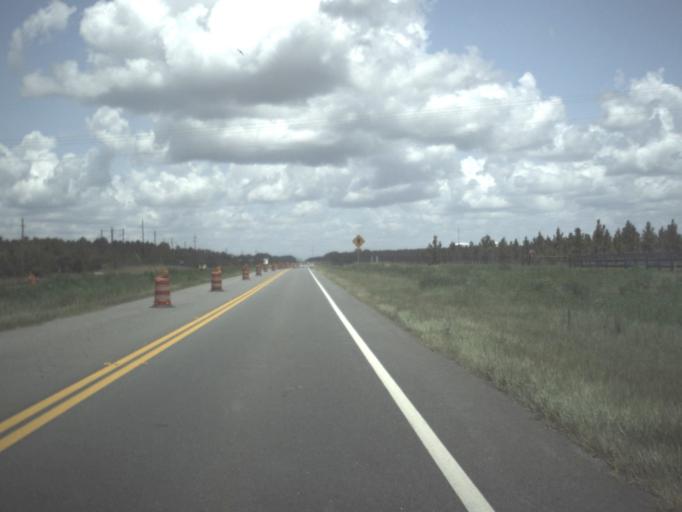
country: US
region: Florida
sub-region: Walton County
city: Freeport
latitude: 30.5610
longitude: -86.1067
